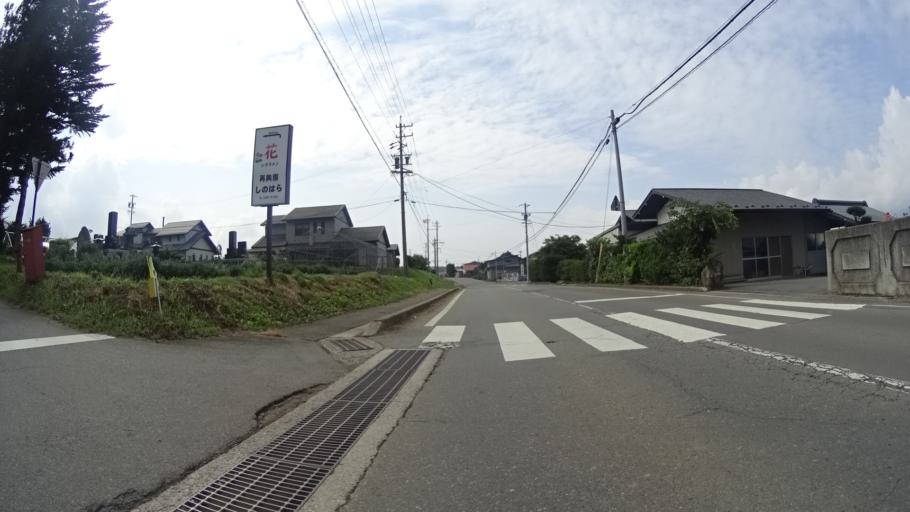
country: JP
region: Nagano
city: Chino
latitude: 35.9509
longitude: 138.2390
